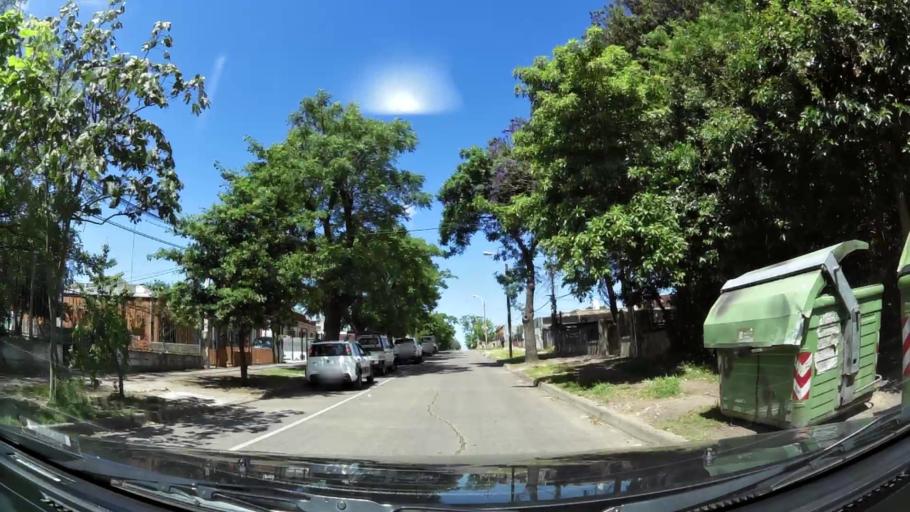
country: UY
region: Montevideo
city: Montevideo
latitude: -34.8547
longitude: -56.1352
